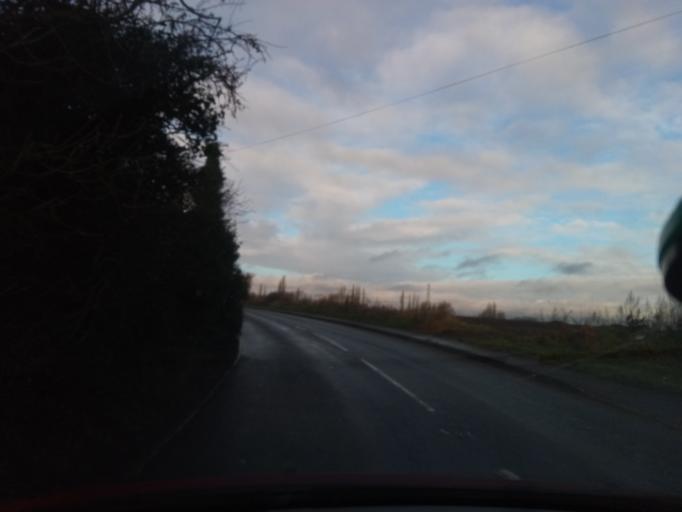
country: GB
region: England
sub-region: Derbyshire
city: Melbourne
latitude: 52.8472
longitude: -1.4087
